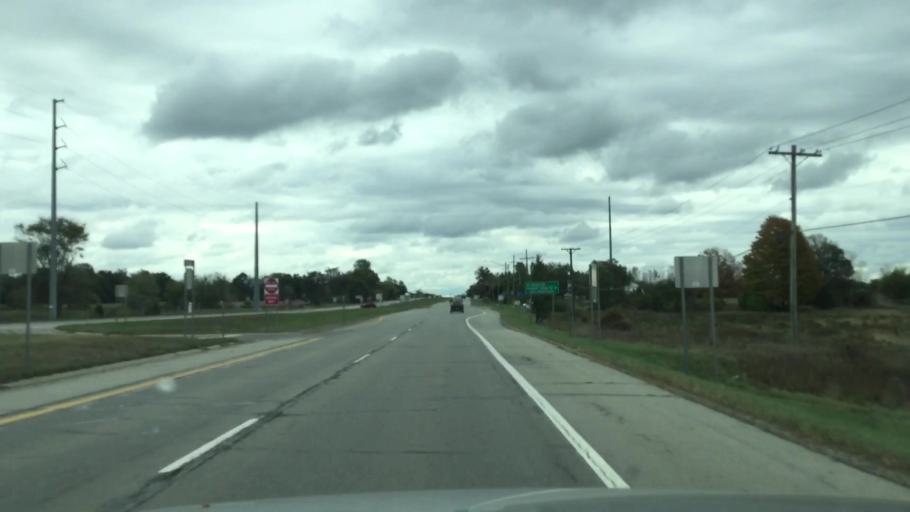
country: US
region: Michigan
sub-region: Oakland County
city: Milford
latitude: 42.6346
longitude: -83.7020
